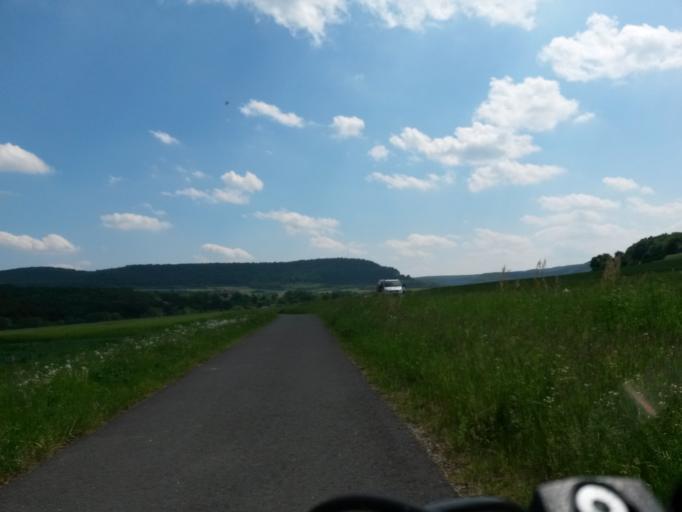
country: DE
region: Bavaria
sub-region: Regierungsbezirk Unterfranken
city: Euerdorf
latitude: 50.1618
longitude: 10.0170
